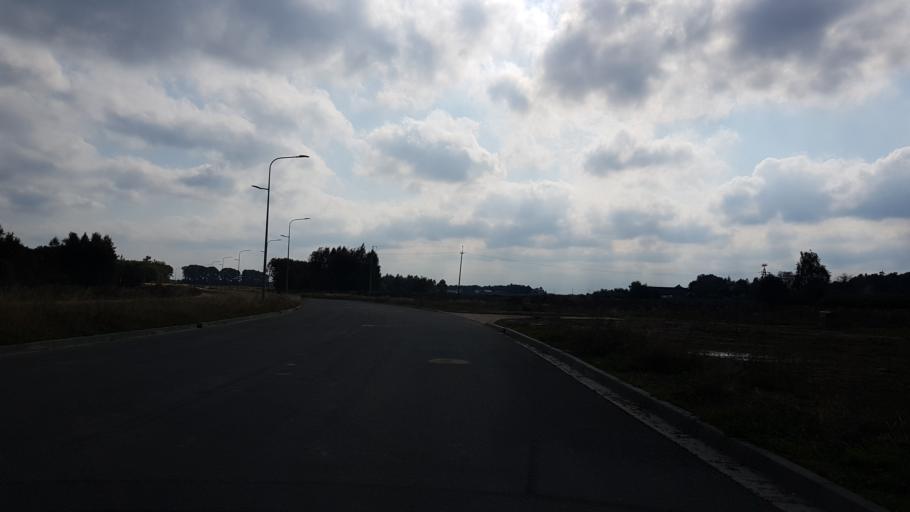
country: PL
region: West Pomeranian Voivodeship
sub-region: Koszalin
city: Koszalin
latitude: 54.1801
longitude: 16.1535
